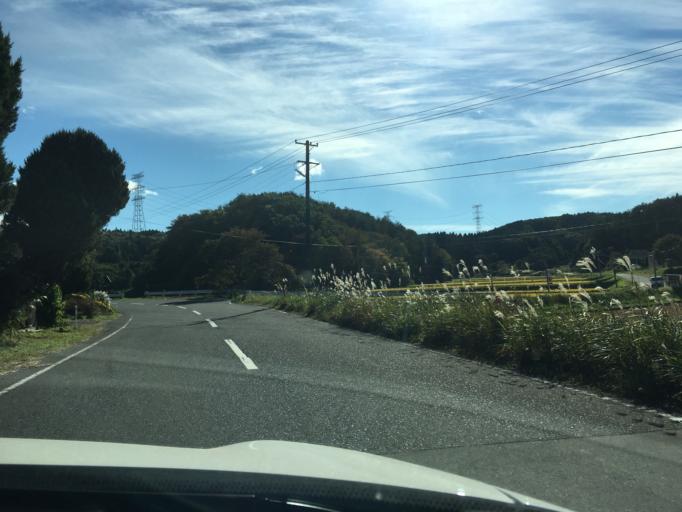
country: JP
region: Fukushima
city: Ishikawa
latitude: 37.1718
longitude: 140.5923
